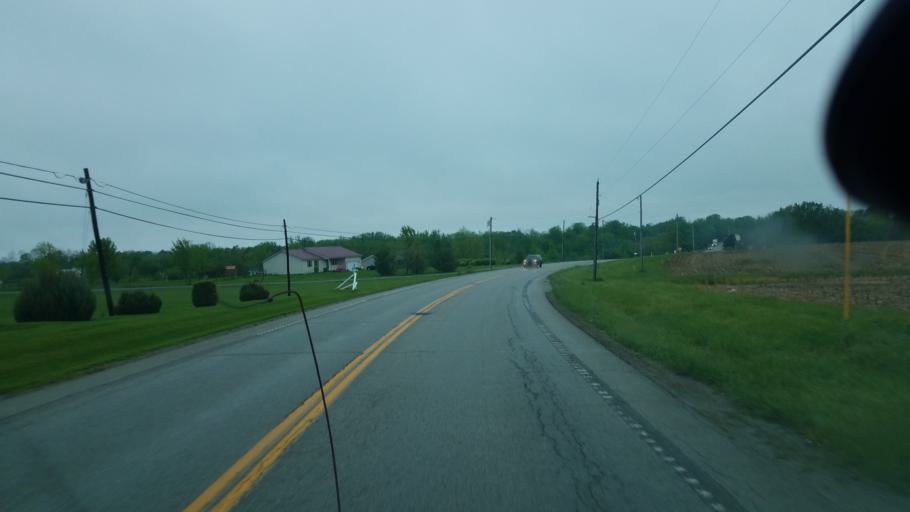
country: US
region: Ohio
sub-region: Highland County
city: Leesburg
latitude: 39.2795
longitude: -83.5941
